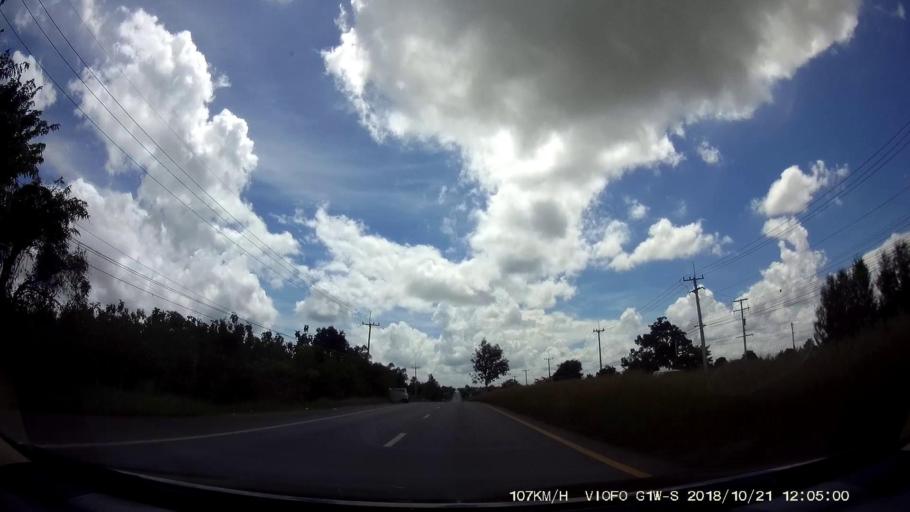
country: TH
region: Chaiyaphum
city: Chatturat
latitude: 15.4856
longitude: 101.8225
